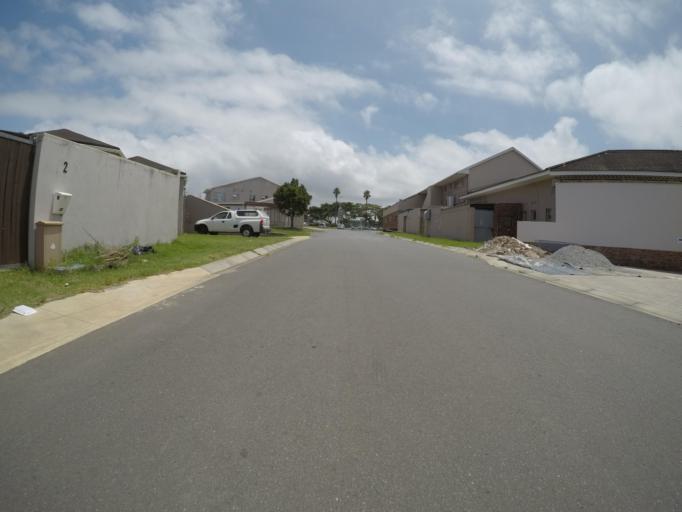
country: ZA
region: Eastern Cape
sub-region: Buffalo City Metropolitan Municipality
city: East London
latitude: -32.9390
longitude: 28.0106
